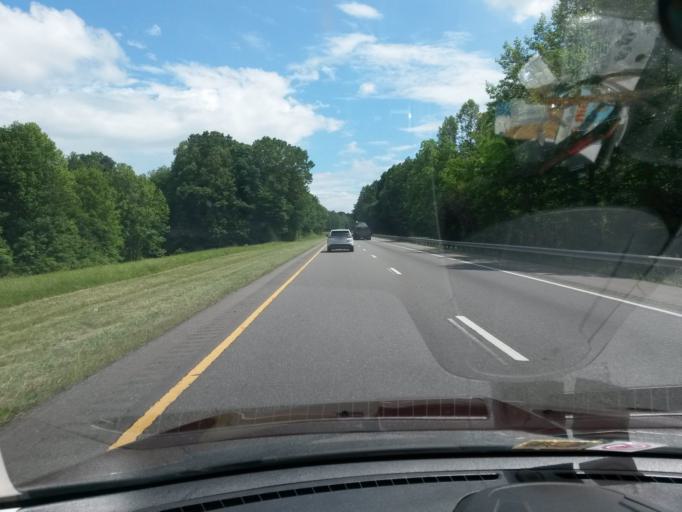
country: US
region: North Carolina
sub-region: Surry County
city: Dobson
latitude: 36.4322
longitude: -80.7774
